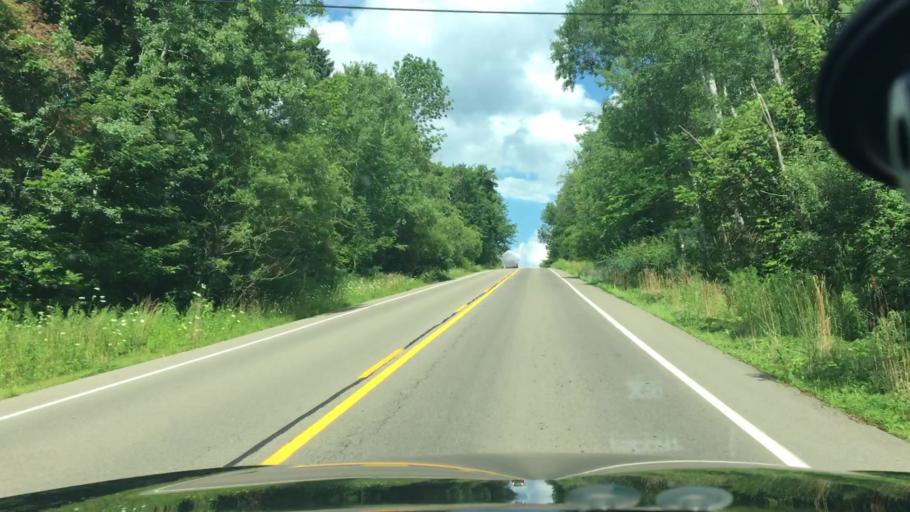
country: US
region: New York
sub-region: Chautauqua County
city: Lakewood
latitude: 42.1793
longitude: -79.3564
